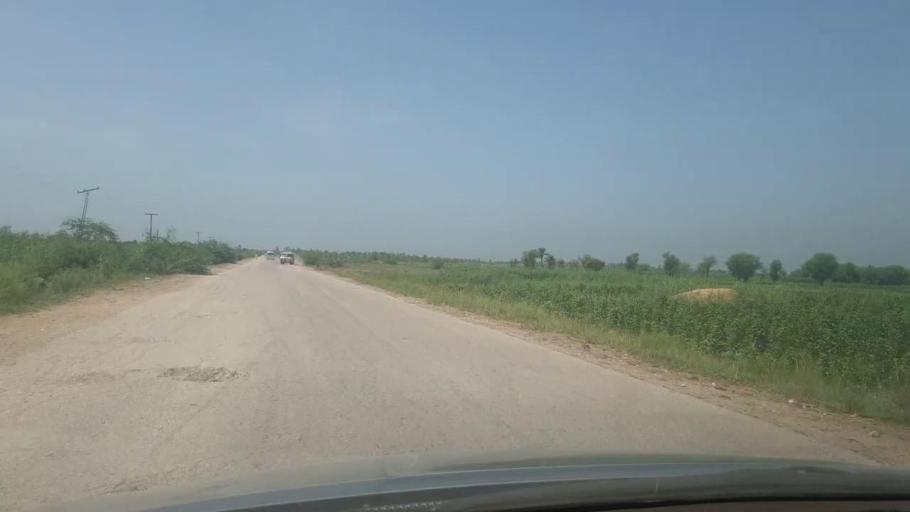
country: PK
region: Sindh
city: Ranipur
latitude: 27.2659
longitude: 68.5924
